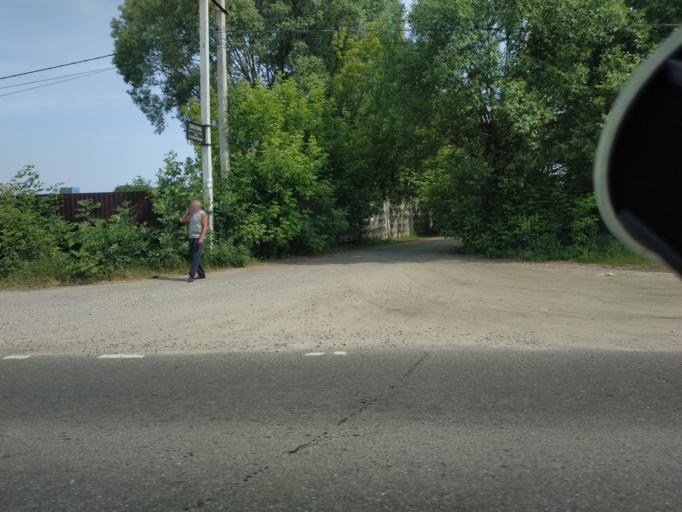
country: RU
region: Moskovskaya
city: Malyshevo
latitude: 55.5372
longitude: 38.3239
